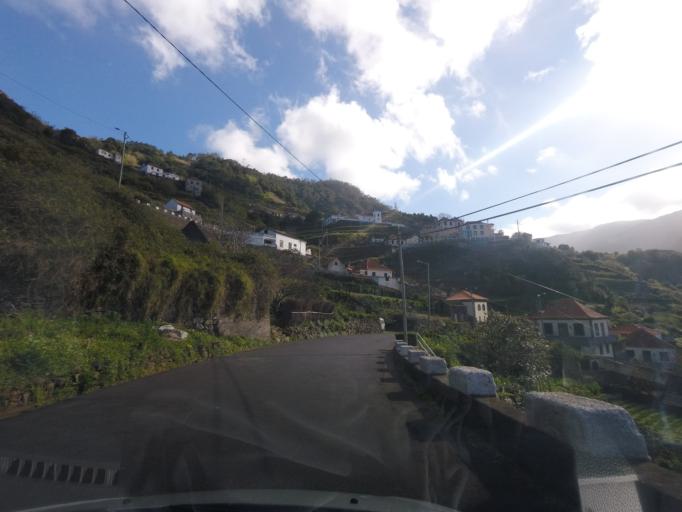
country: PT
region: Madeira
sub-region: Porto Moniz
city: Porto Moniz
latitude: 32.8489
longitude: -17.1574
